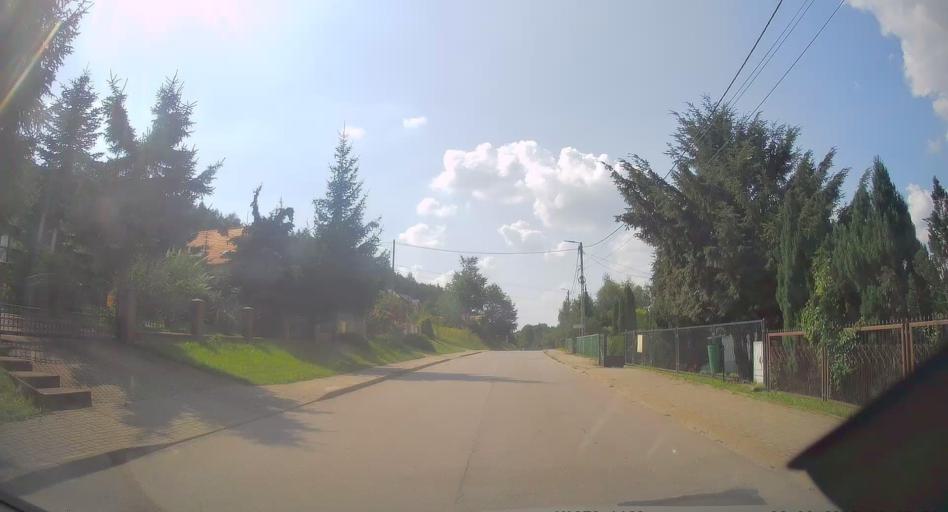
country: PL
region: Swietokrzyskie
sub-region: Powiat kielecki
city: Checiny
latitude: 50.8023
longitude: 20.4547
